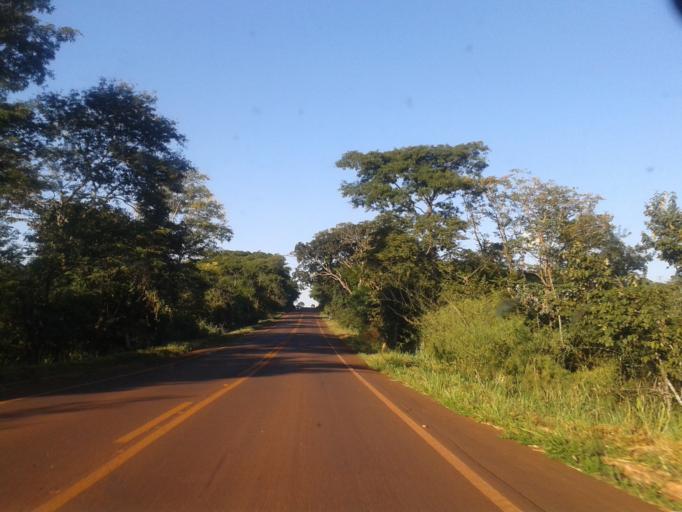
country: BR
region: Minas Gerais
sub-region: Capinopolis
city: Capinopolis
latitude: -18.6887
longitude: -49.6102
